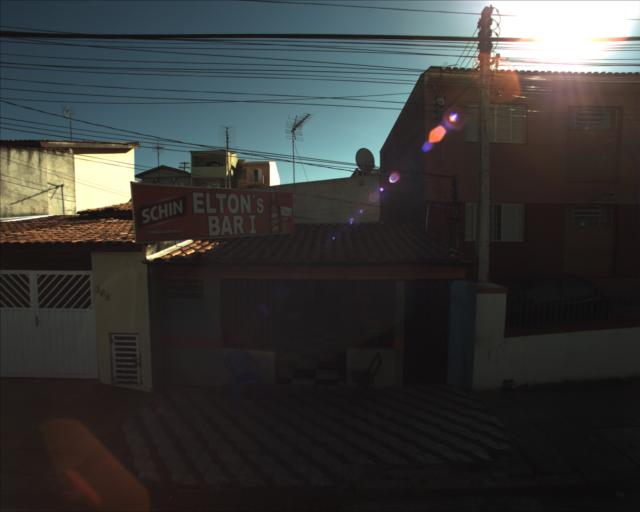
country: BR
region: Sao Paulo
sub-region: Sorocaba
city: Sorocaba
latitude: -23.5077
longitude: -47.4783
